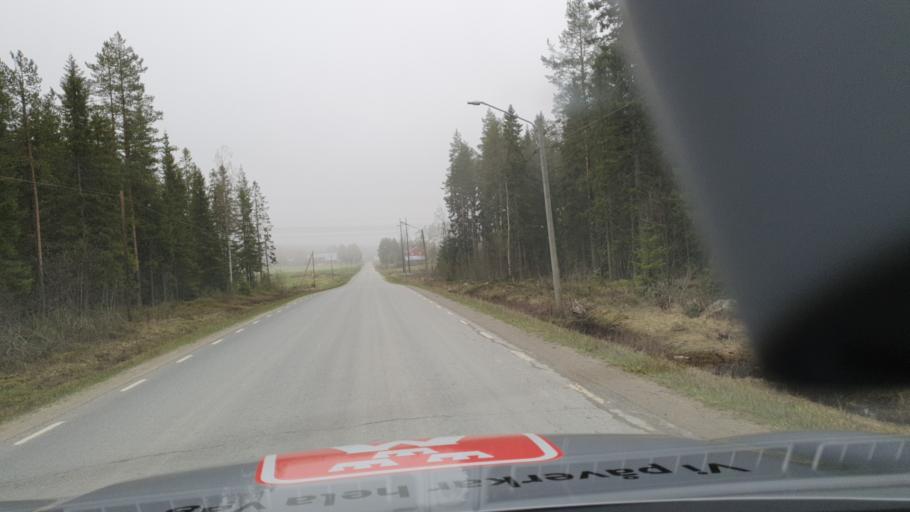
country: SE
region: Vaesternorrland
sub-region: OErnskoeldsviks Kommun
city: Husum
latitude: 63.5874
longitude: 19.0198
